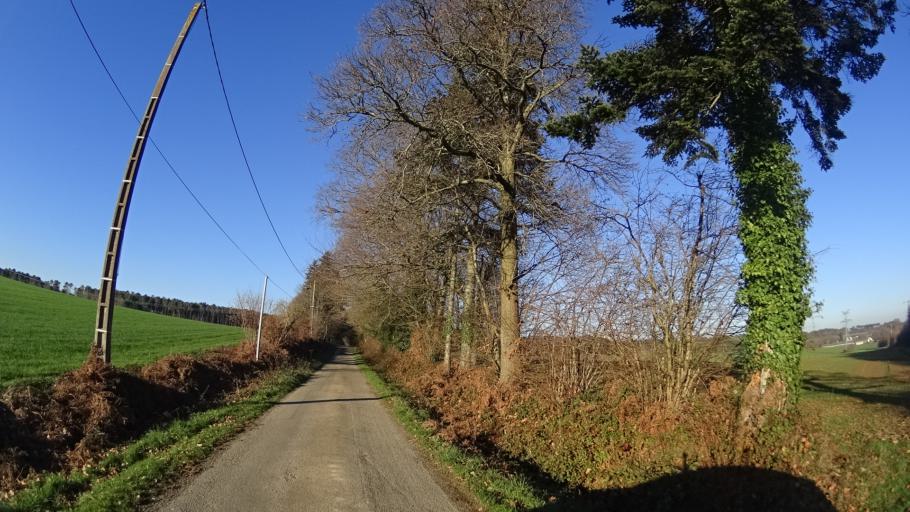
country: FR
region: Brittany
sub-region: Departement du Morbihan
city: Saint-Jacut-les-Pins
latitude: 47.6724
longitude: -2.1814
